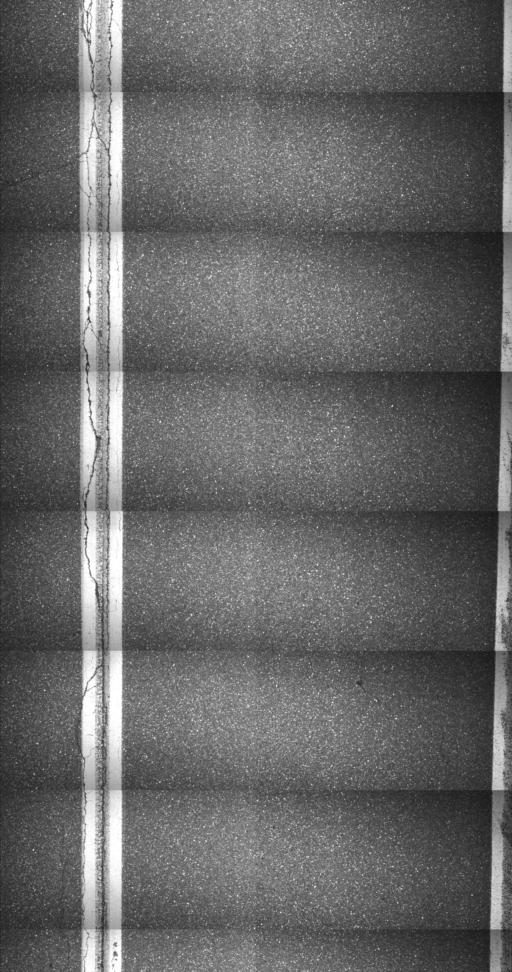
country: US
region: Vermont
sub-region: Washington County
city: Barre
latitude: 44.2845
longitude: -72.2954
